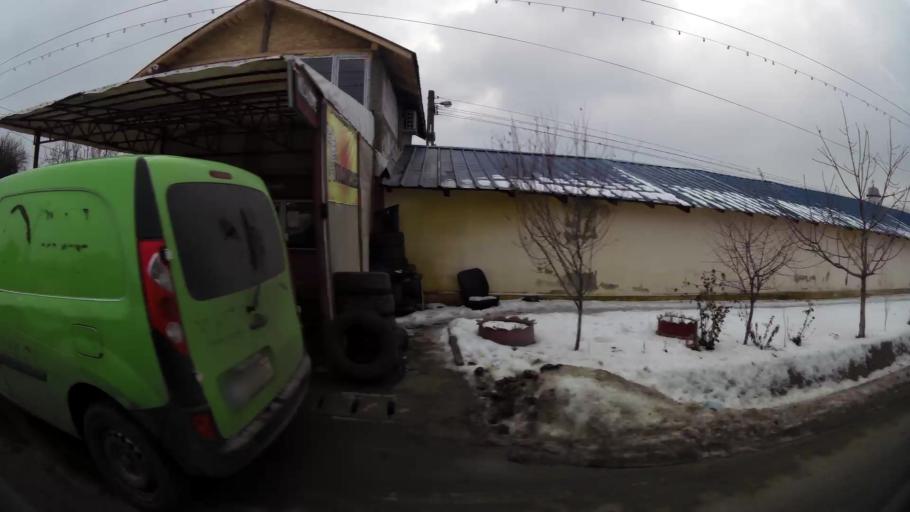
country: RO
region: Ilfov
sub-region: Comuna Afumati
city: Afumati
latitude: 44.5267
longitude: 26.2438
